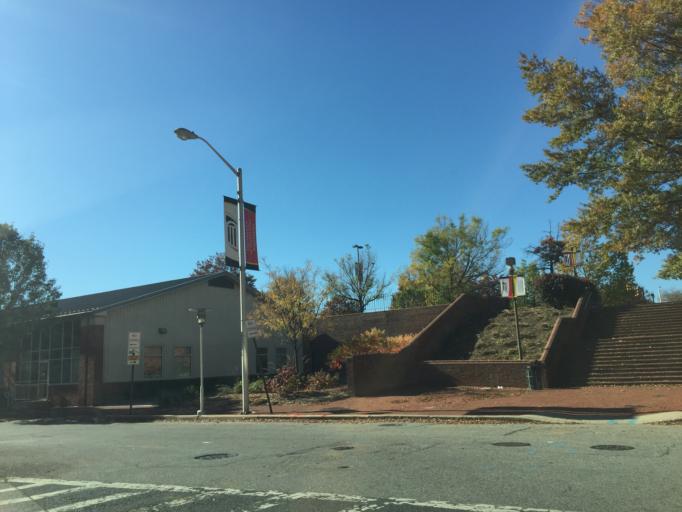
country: US
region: Maryland
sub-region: City of Baltimore
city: Baltimore
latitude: 39.2913
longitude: -76.6268
